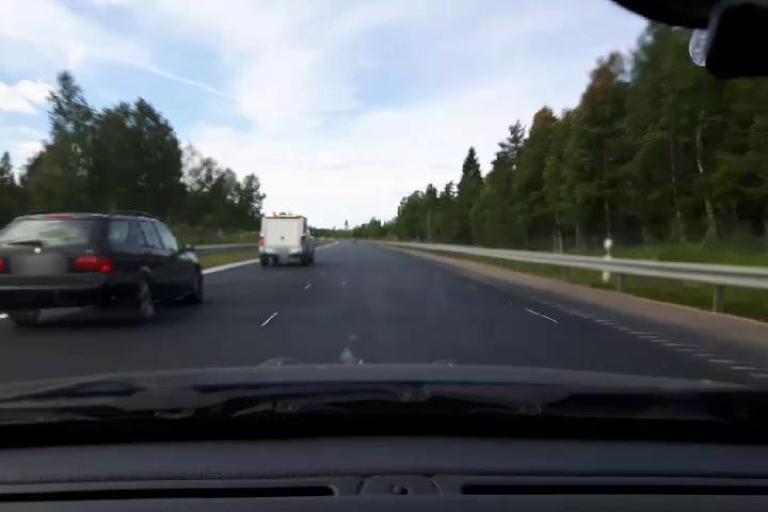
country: SE
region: Gaevleborg
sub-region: Gavle Kommun
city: Gavle
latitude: 60.5795
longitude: 17.2176
